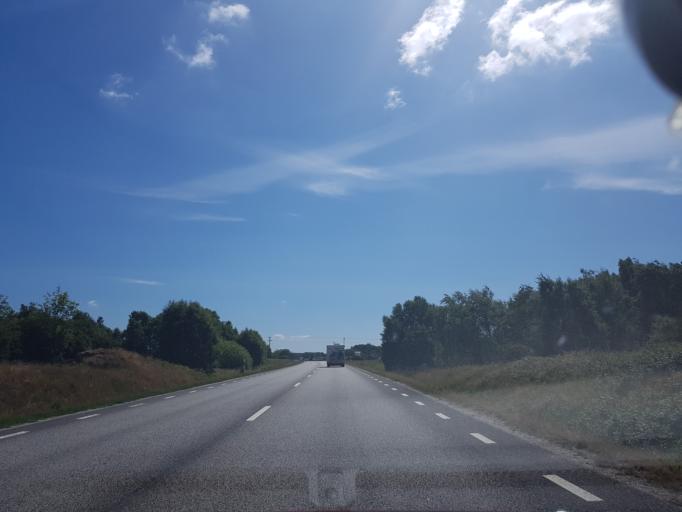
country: SE
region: Vaestra Goetaland
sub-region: Orust
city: Henan
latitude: 58.1524
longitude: 11.5742
